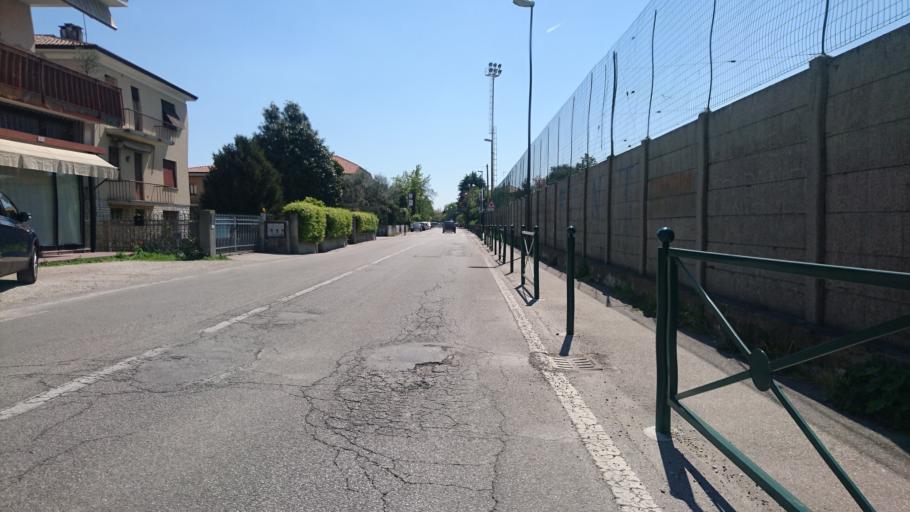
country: IT
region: Veneto
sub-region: Provincia di Treviso
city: Dosson
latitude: 45.6584
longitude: 12.2563
